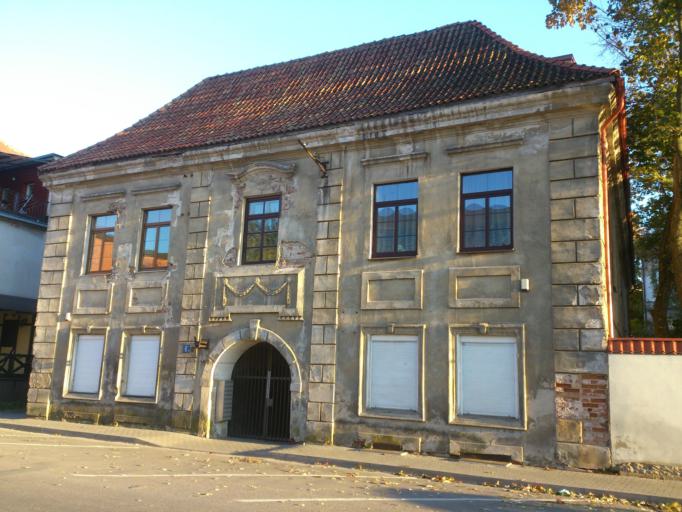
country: LT
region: Kauno apskritis
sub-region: Kaunas
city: Kaunas
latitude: 54.8997
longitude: 23.8906
